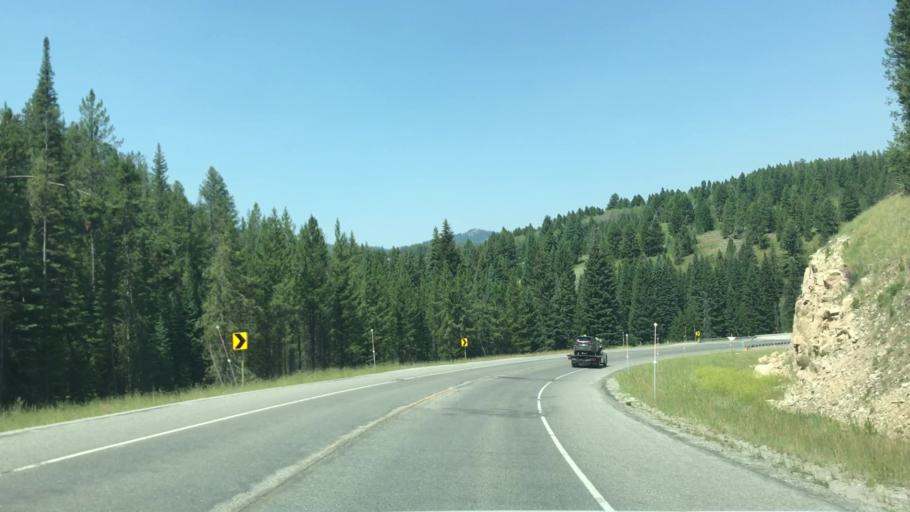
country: US
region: Montana
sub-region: Gallatin County
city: West Yellowstone
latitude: 44.8006
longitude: -111.1074
